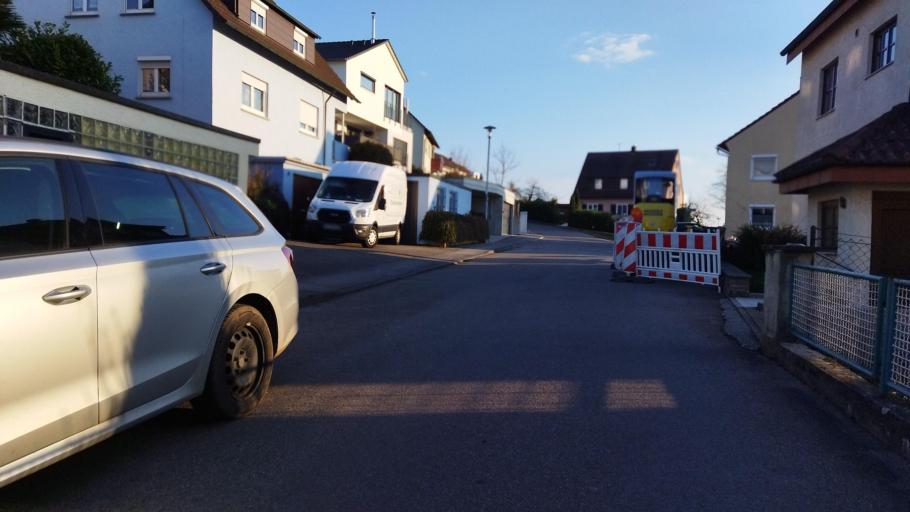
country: DE
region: Baden-Wuerttemberg
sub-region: Regierungsbezirk Stuttgart
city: Gemmrigheim
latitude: 49.0232
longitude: 9.1592
